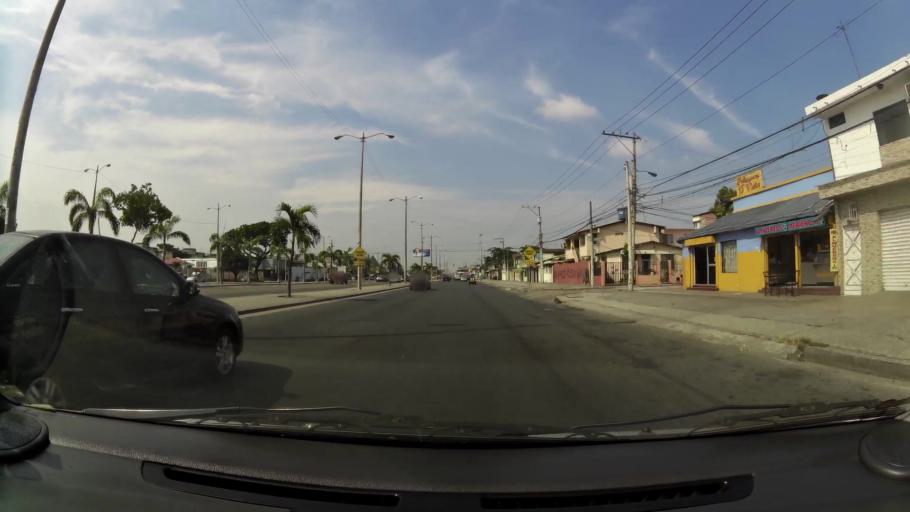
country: EC
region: Guayas
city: Guayaquil
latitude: -2.2444
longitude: -79.8957
